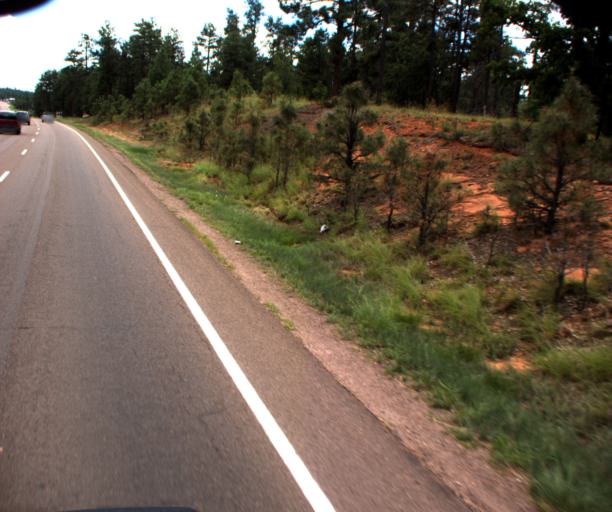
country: US
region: Arizona
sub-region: Navajo County
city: Lake of the Woods
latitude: 34.1792
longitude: -110.0120
